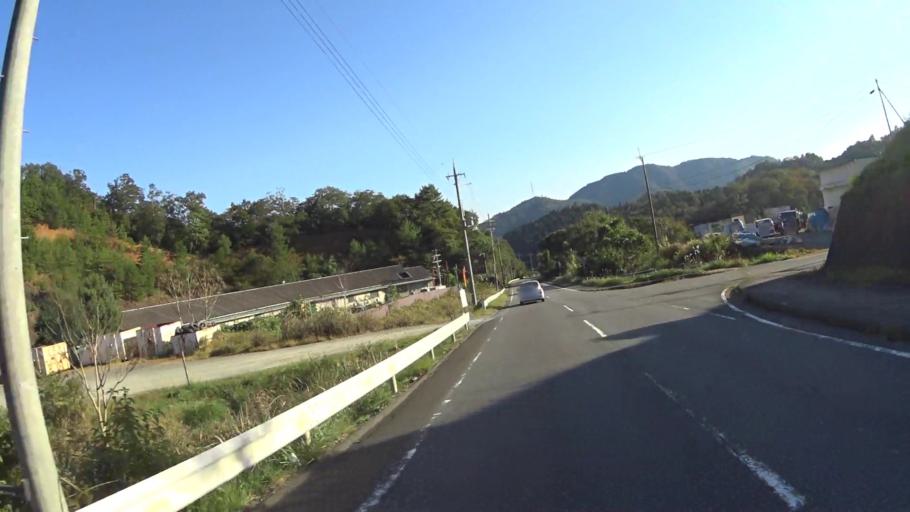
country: JP
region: Kyoto
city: Fukuchiyama
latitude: 35.3747
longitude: 135.0993
